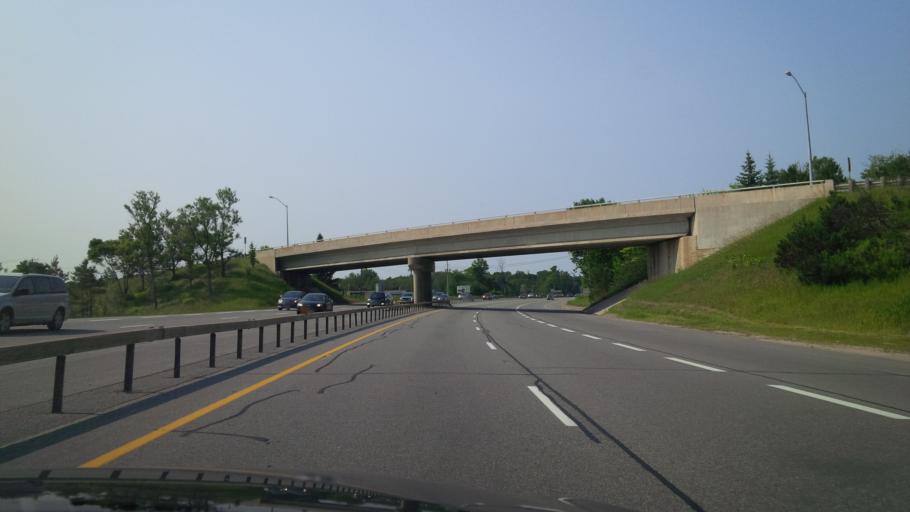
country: CA
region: Ontario
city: Orillia
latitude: 44.5659
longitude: -79.4428
